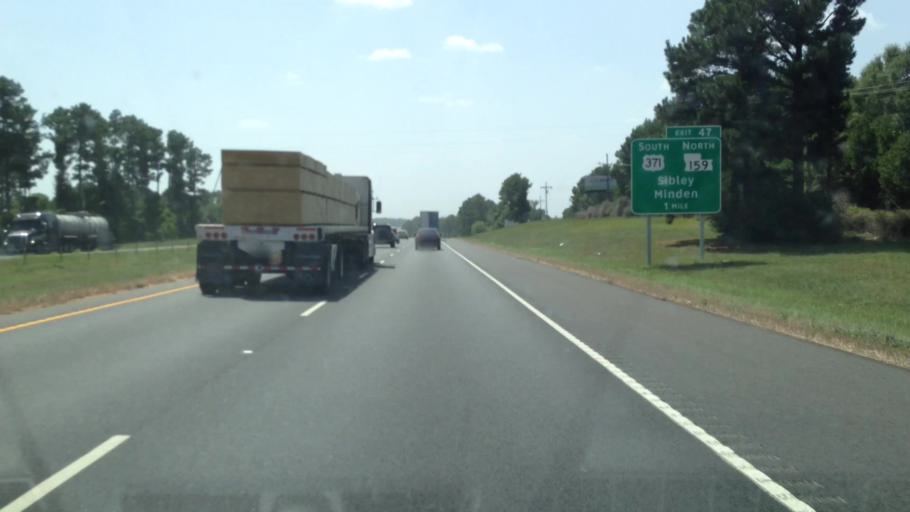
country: US
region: Louisiana
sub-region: Webster Parish
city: Minden
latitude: 32.5854
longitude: -93.2713
